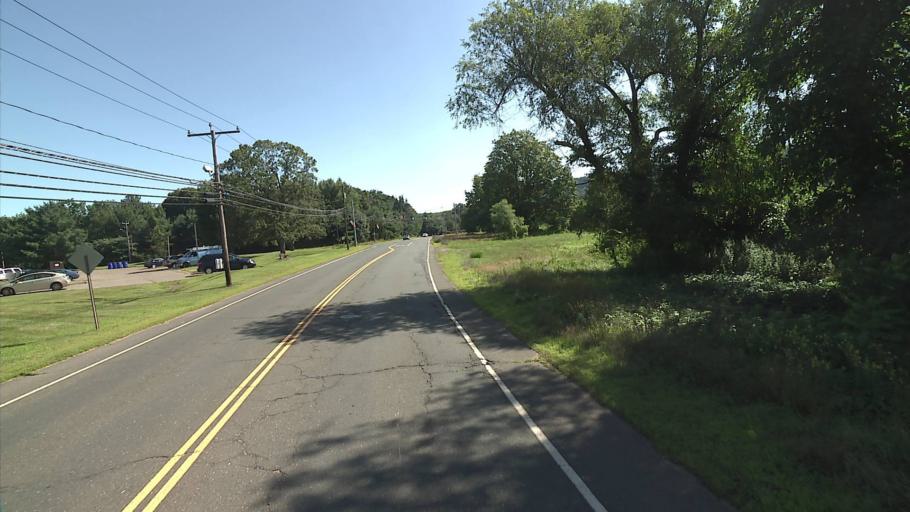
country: US
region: Connecticut
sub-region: Hartford County
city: Weatogue
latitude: 41.8273
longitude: -72.8262
